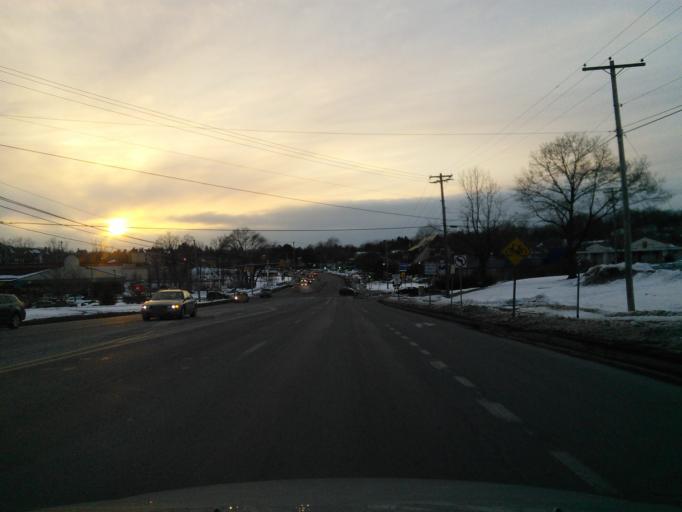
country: US
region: Pennsylvania
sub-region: Centre County
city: State College
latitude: 40.7851
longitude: -77.8330
